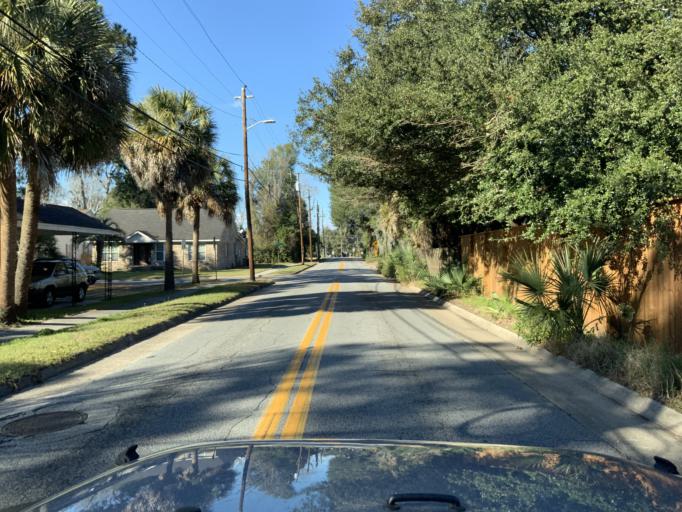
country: US
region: Georgia
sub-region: Chatham County
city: Thunderbolt
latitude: 32.0584
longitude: -81.0693
